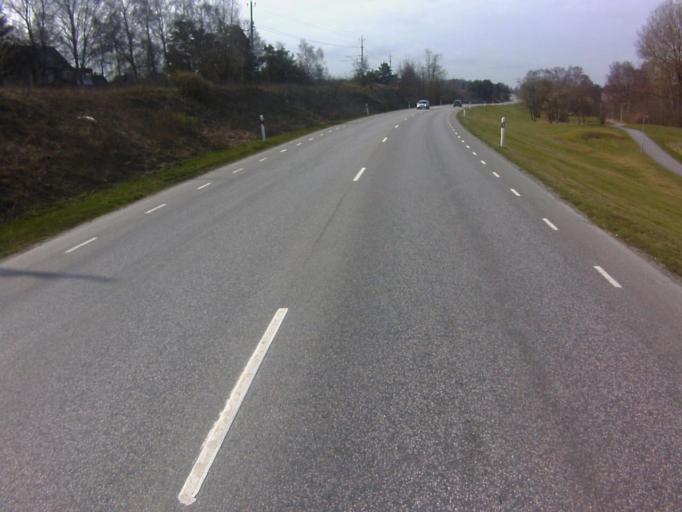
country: SE
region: Skane
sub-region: Kavlinge Kommun
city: Kaevlinge
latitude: 55.7826
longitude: 13.1072
